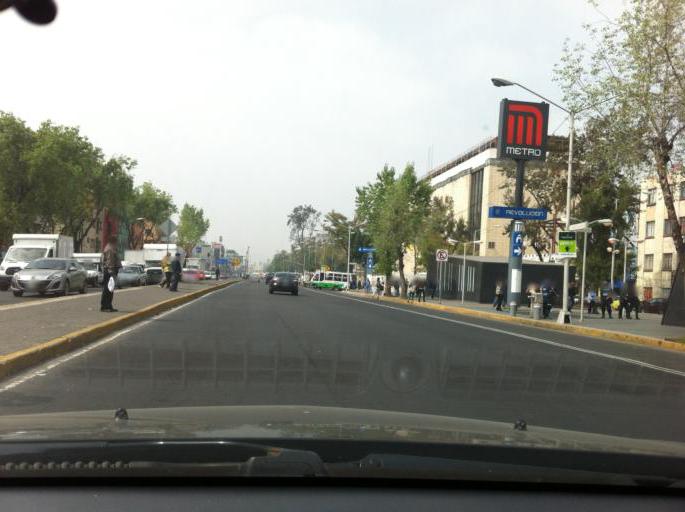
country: MX
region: Mexico City
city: Cuauhtemoc
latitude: 19.4391
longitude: -99.1540
